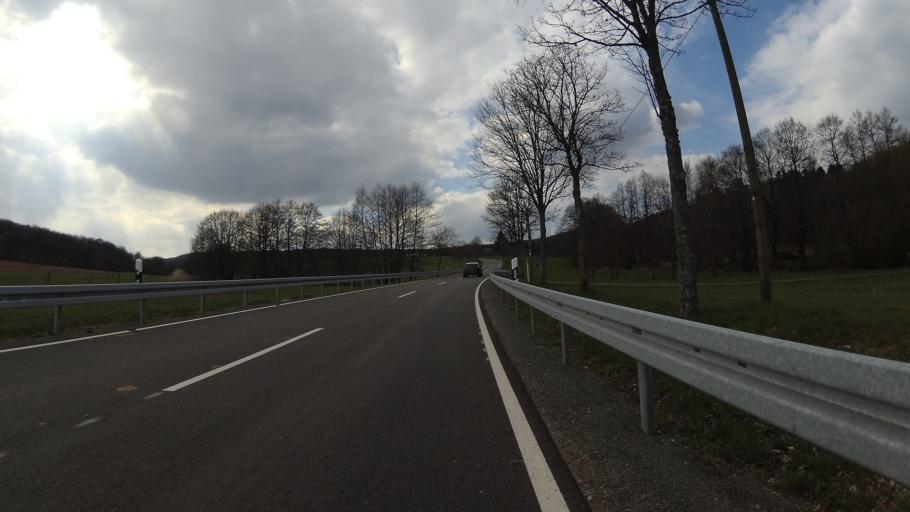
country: DE
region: Saarland
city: Oberthal
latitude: 49.5477
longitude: 7.0512
